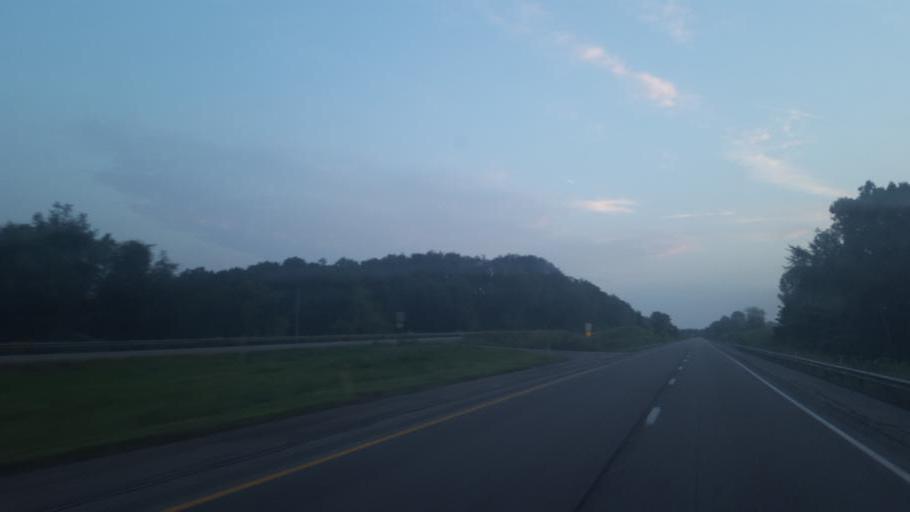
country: US
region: Pennsylvania
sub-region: Mercer County
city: Stoneboro
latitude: 41.4345
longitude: -80.1631
